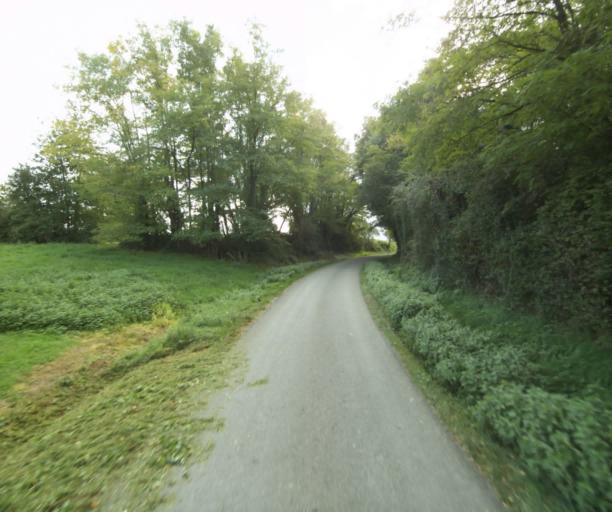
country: FR
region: Midi-Pyrenees
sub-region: Departement du Gers
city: Eauze
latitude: 43.8920
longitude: 0.0802
